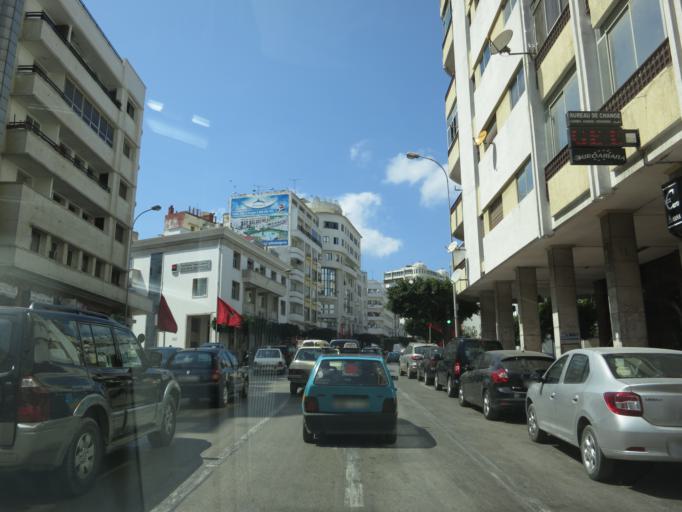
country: MA
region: Tanger-Tetouan
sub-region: Tanger-Assilah
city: Tangier
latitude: 35.7777
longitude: -5.8065
